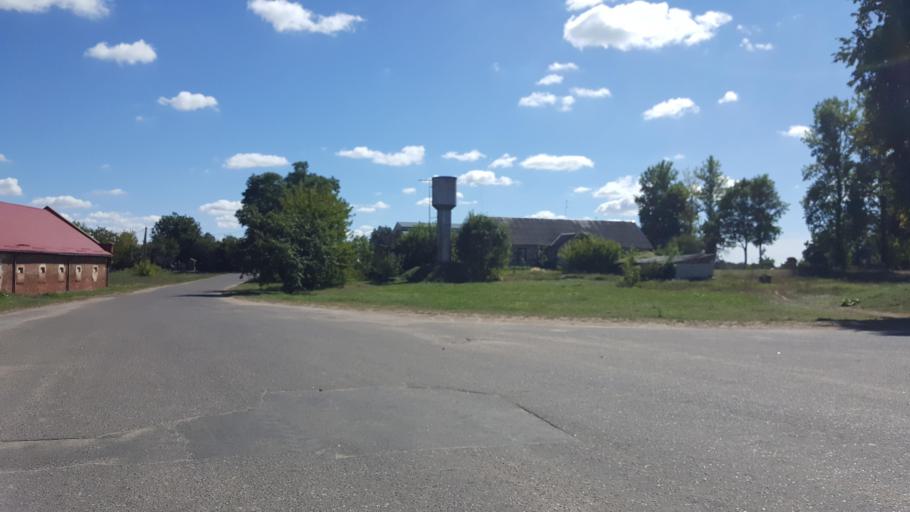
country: BY
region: Brest
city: Vysokaye
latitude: 52.3492
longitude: 23.3434
